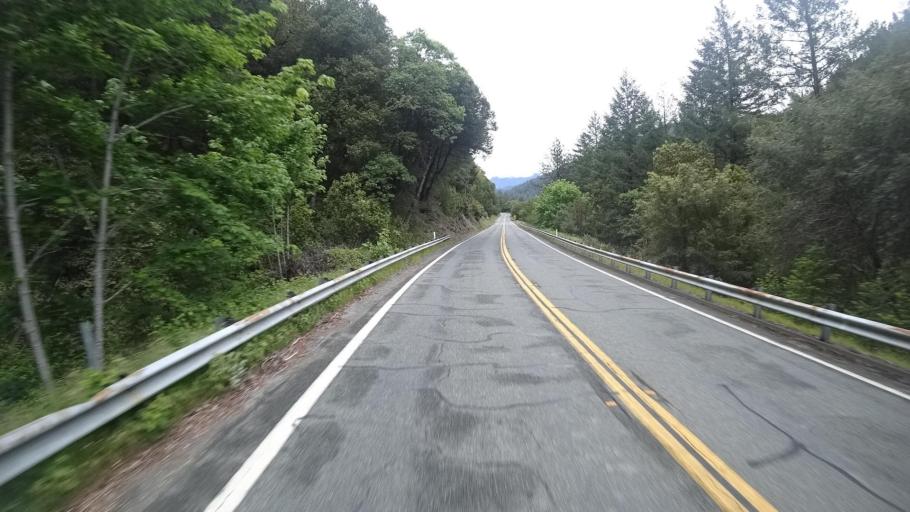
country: US
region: California
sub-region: Humboldt County
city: Willow Creek
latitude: 41.2602
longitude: -123.6139
